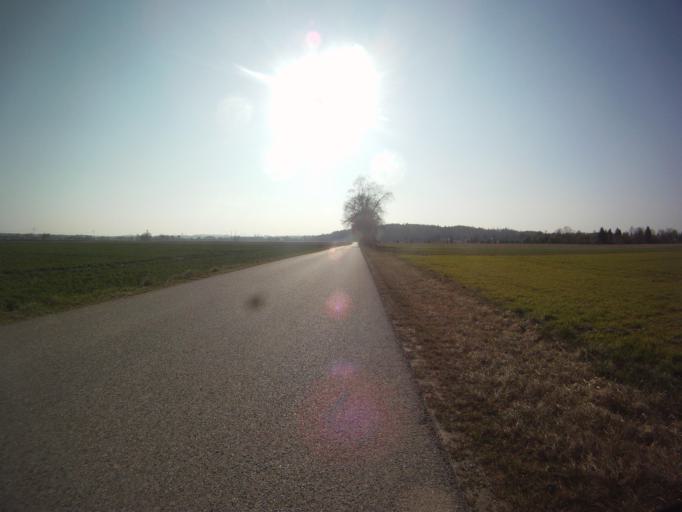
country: DE
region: Bavaria
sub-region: Upper Bavaria
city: Haiming
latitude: 48.2220
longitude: 12.8851
